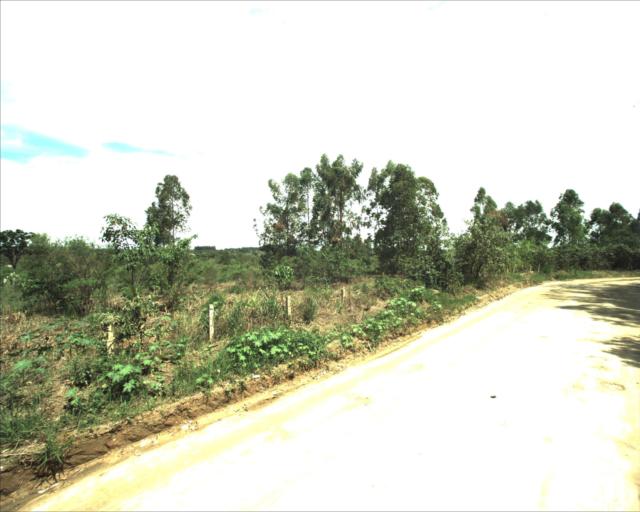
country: BR
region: Sao Paulo
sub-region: Aracoiaba Da Serra
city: Aracoiaba da Serra
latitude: -23.5547
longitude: -47.5414
